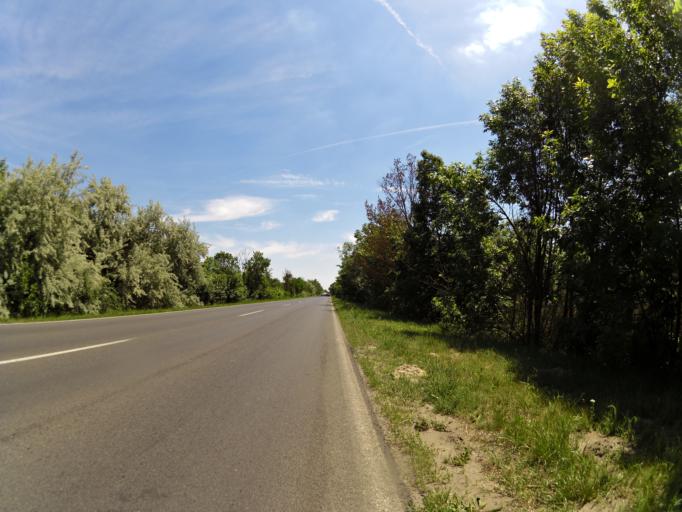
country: HU
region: Csongrad
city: Szatymaz
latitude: 46.3103
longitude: 20.0667
